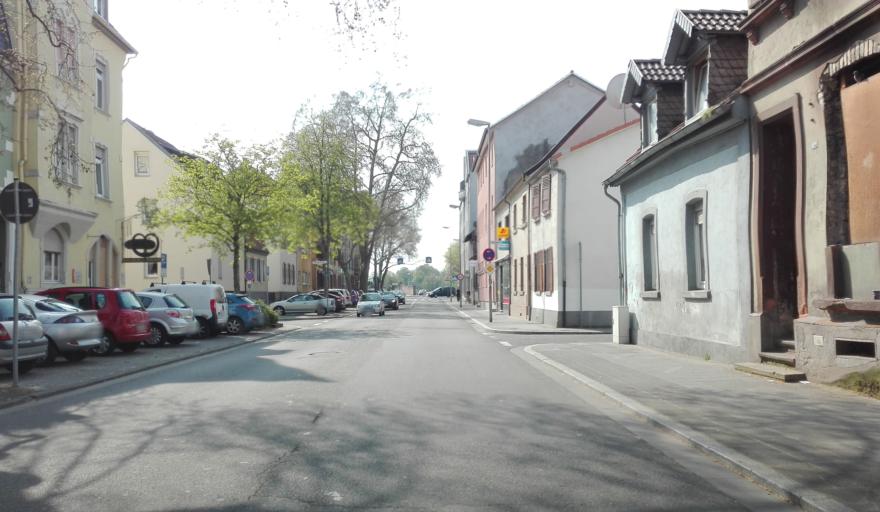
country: DE
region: Rheinland-Pfalz
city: Frankenthal
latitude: 49.5366
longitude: 8.3600
